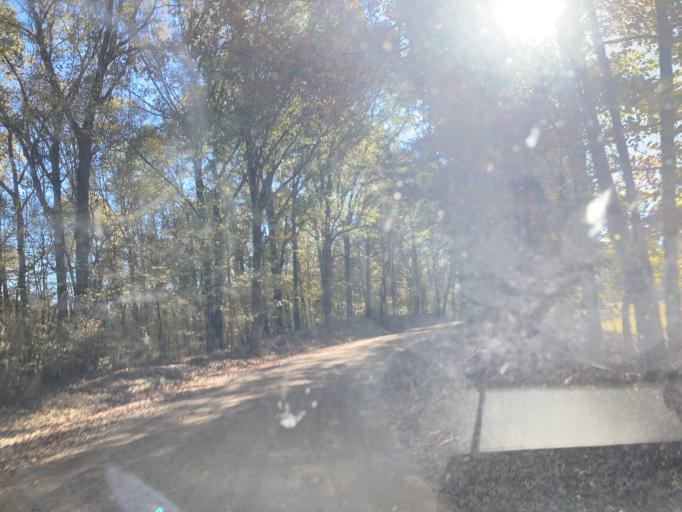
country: US
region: Mississippi
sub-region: Yazoo County
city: Yazoo City
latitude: 32.7565
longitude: -90.3881
